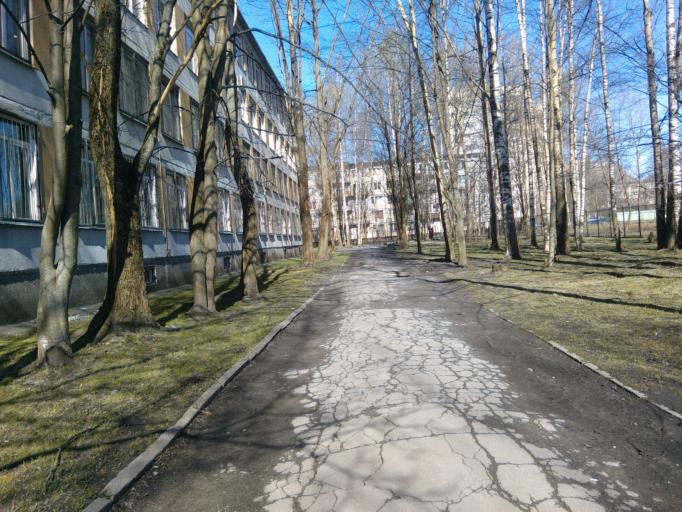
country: RU
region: St.-Petersburg
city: Grazhdanka
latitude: 60.0313
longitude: 30.4096
